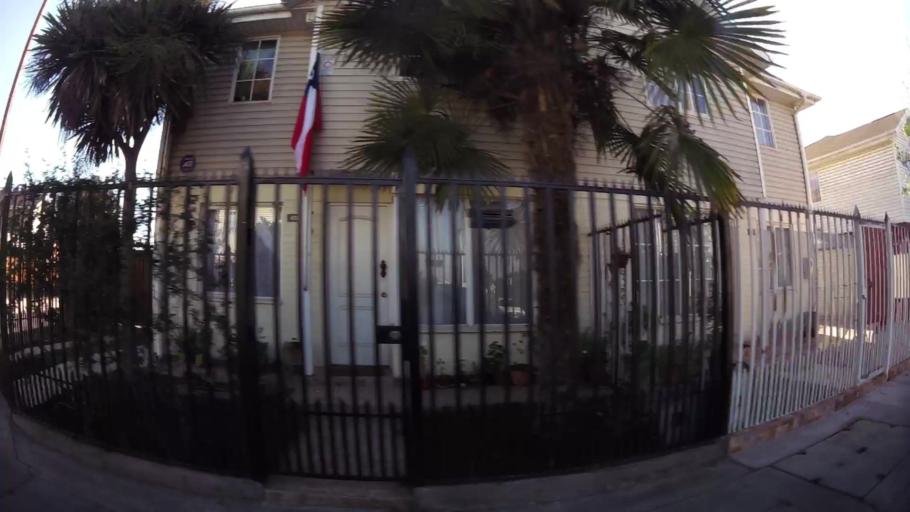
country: CL
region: Santiago Metropolitan
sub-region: Provincia de Santiago
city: Lo Prado
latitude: -33.4935
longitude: -70.7817
